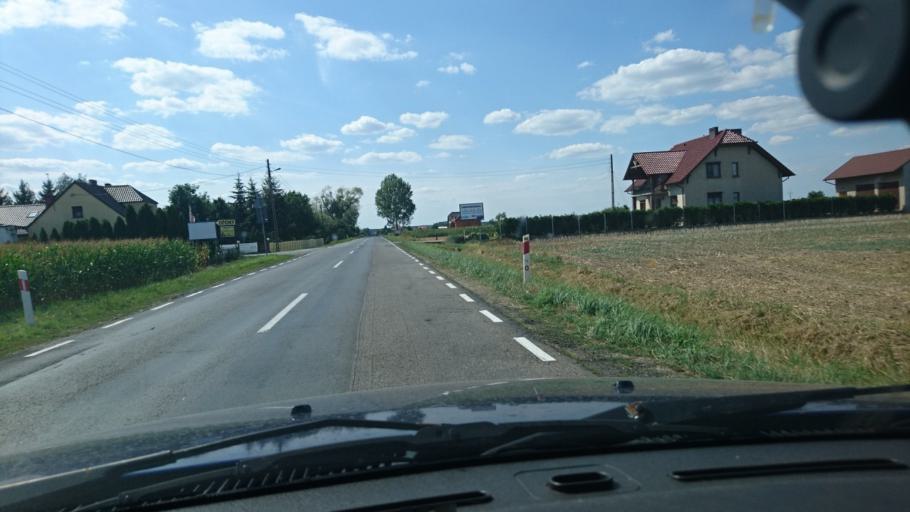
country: PL
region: Greater Poland Voivodeship
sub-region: Powiat krotoszynski
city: Sulmierzyce
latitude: 51.6053
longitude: 17.5522
